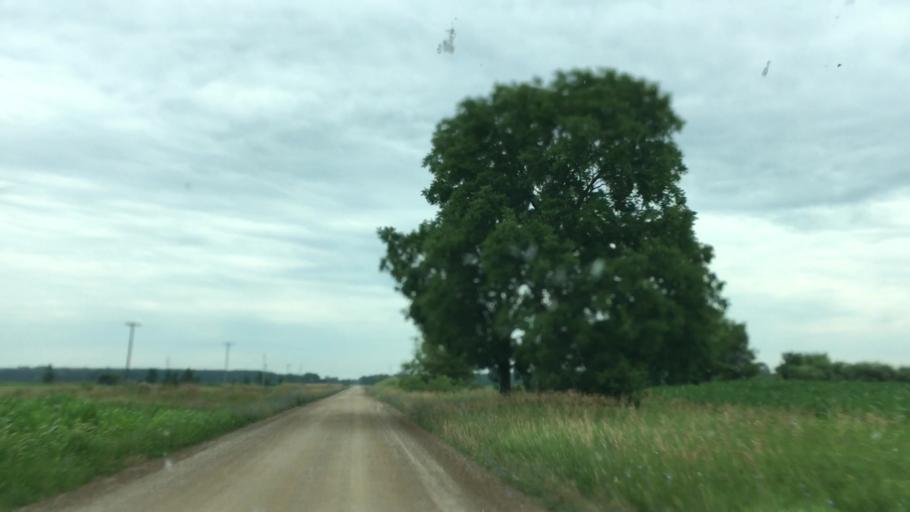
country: US
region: Michigan
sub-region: Clinton County
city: Saint Johns
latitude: 43.0702
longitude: -84.4840
